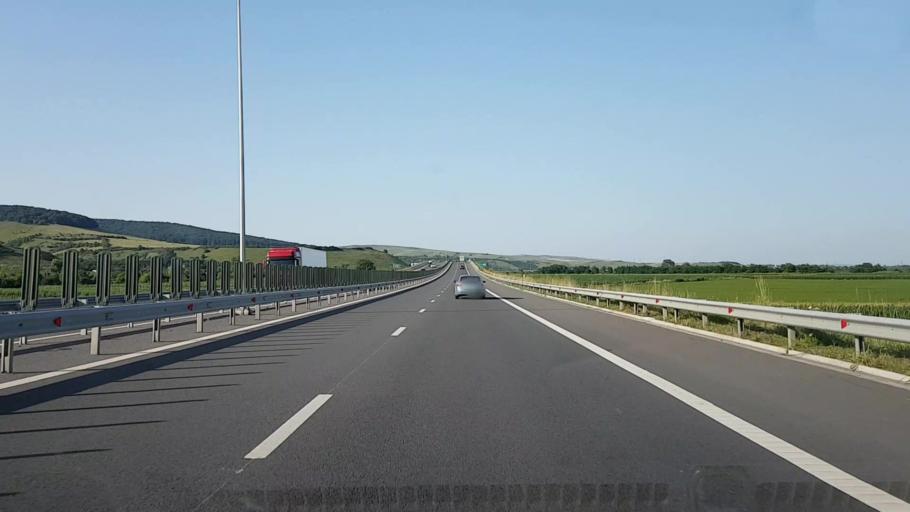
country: RO
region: Alba
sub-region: Comuna Miraslau
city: Miraslau
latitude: 46.3671
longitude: 23.7376
